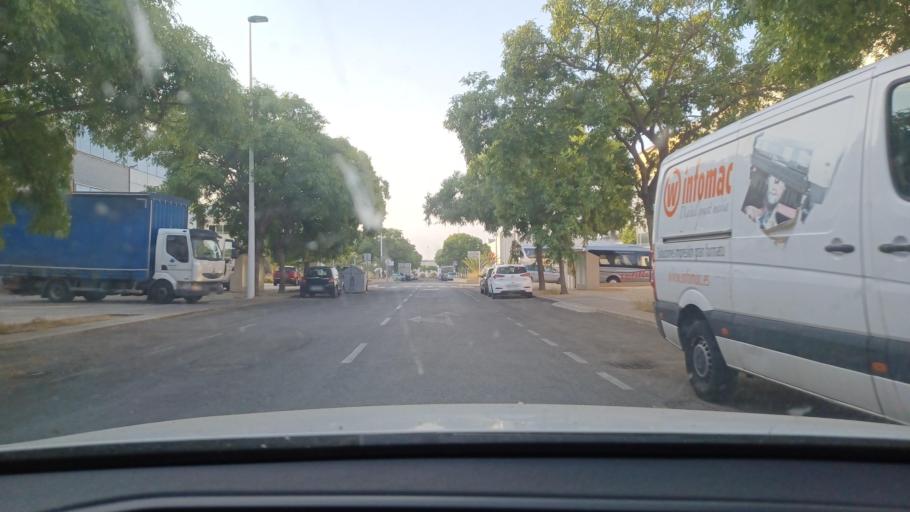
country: ES
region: Valencia
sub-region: Provincia de Alicante
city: Elche
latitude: 38.2945
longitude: -0.6199
